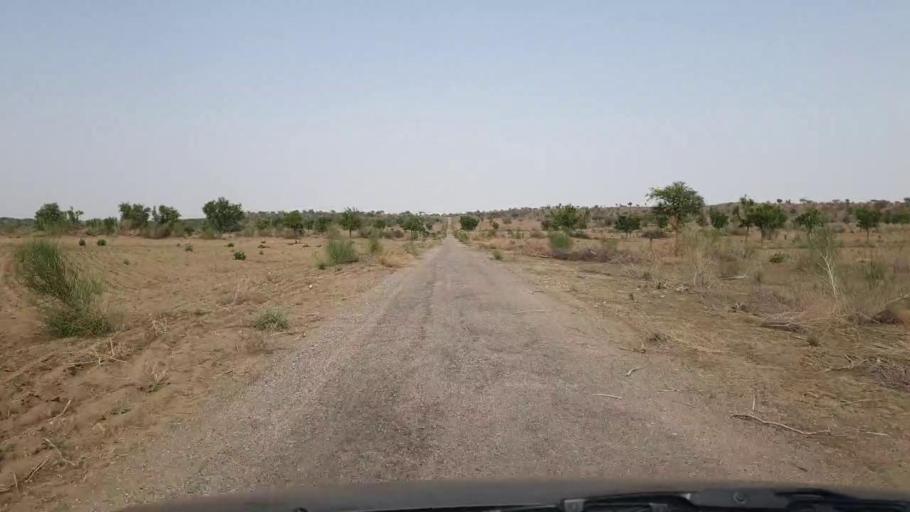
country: PK
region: Sindh
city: Chor
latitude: 25.4817
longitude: 70.5460
